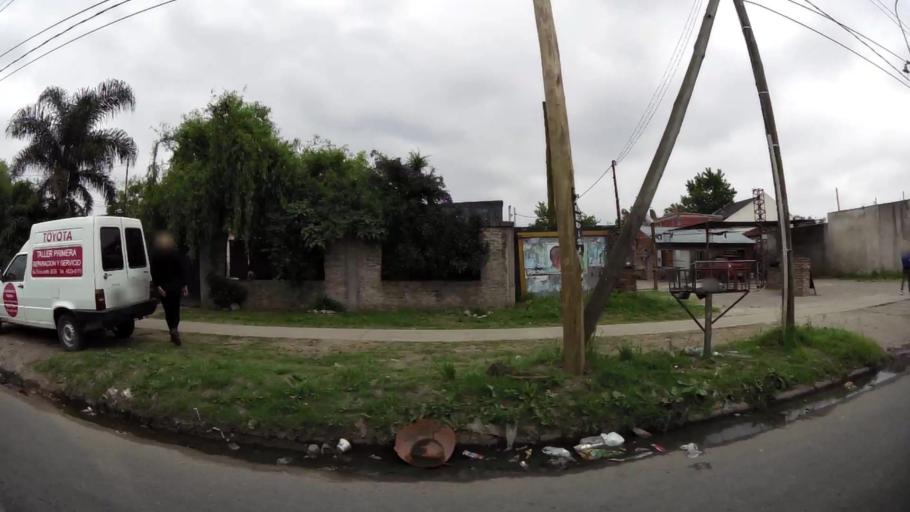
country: AR
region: Buenos Aires
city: San Justo
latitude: -34.7268
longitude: -58.5245
